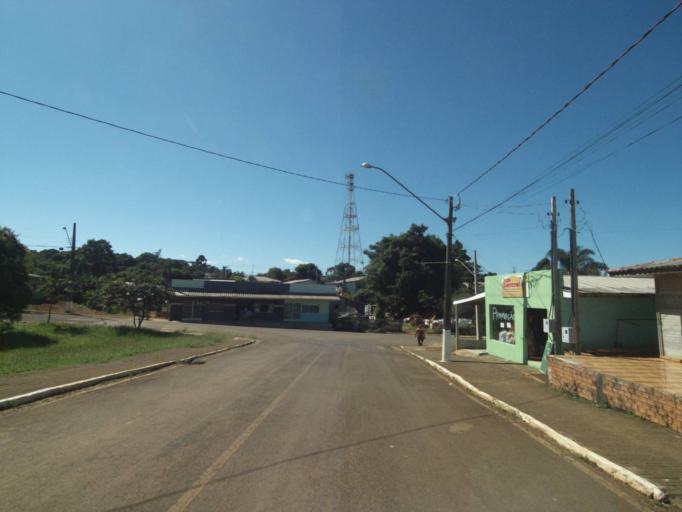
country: BR
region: Parana
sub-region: Pinhao
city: Pinhao
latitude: -25.8372
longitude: -52.0283
